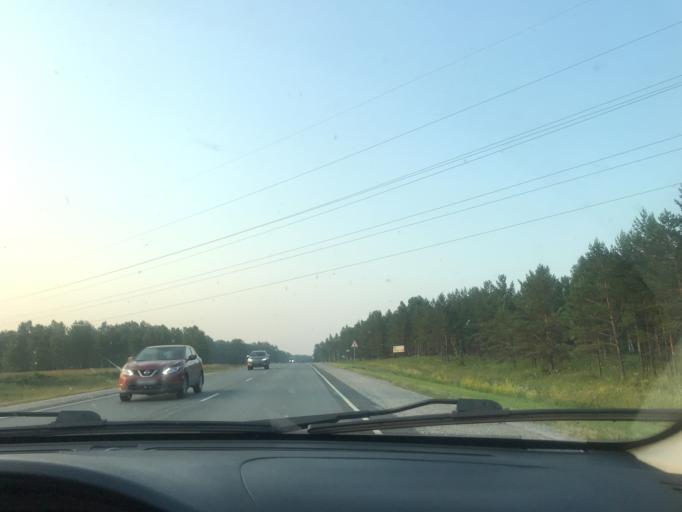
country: RU
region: Novosibirsk
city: Dorogino
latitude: 54.3767
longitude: 83.3062
